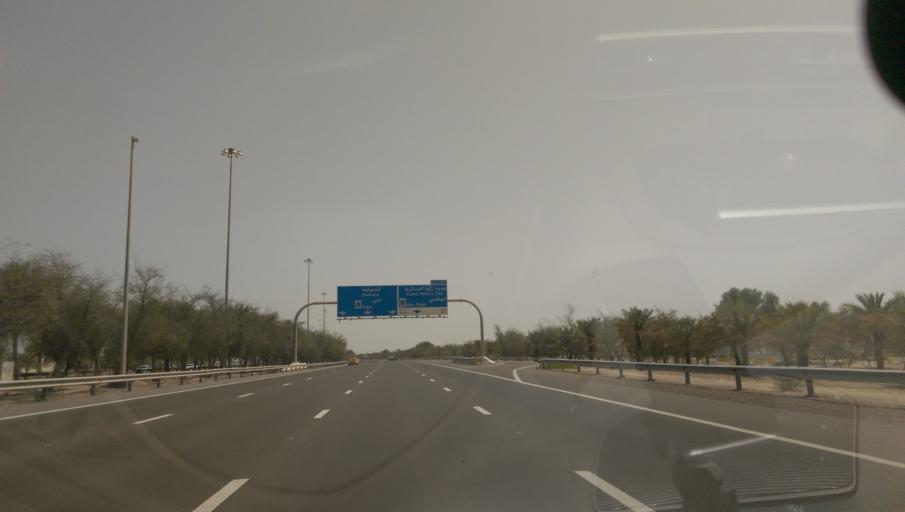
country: AE
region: Abu Dhabi
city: Abu Dhabi
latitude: 24.5184
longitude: 54.6900
